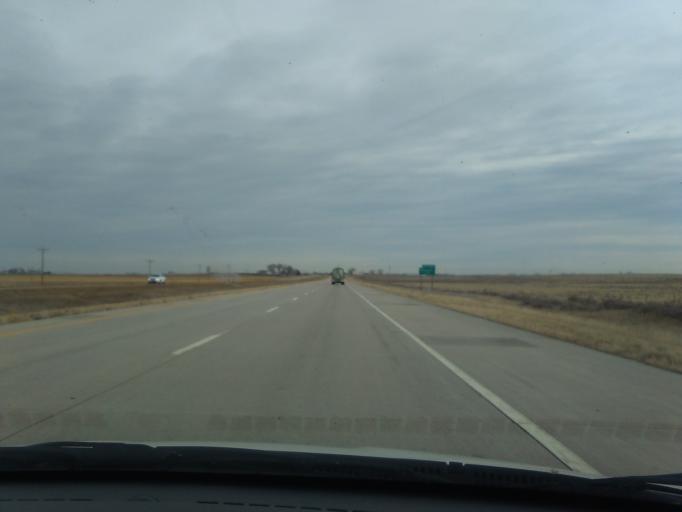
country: US
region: Colorado
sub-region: Morgan County
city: Fort Morgan
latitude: 40.2322
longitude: -104.1174
